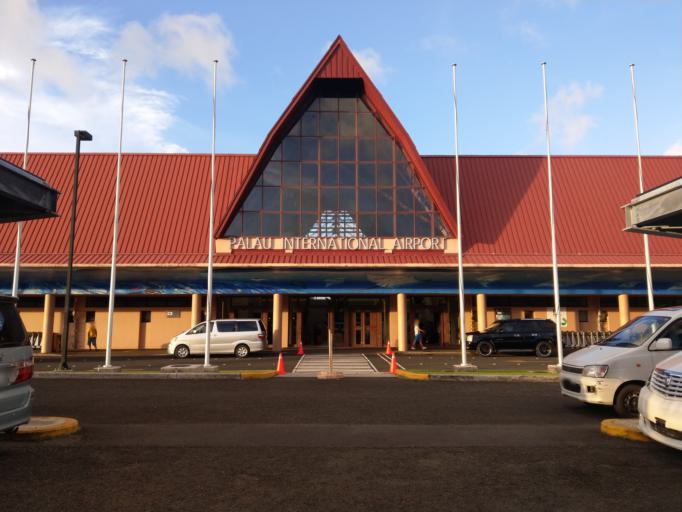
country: PW
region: Airai
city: Ngetkib
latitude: 7.3639
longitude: 134.5329
